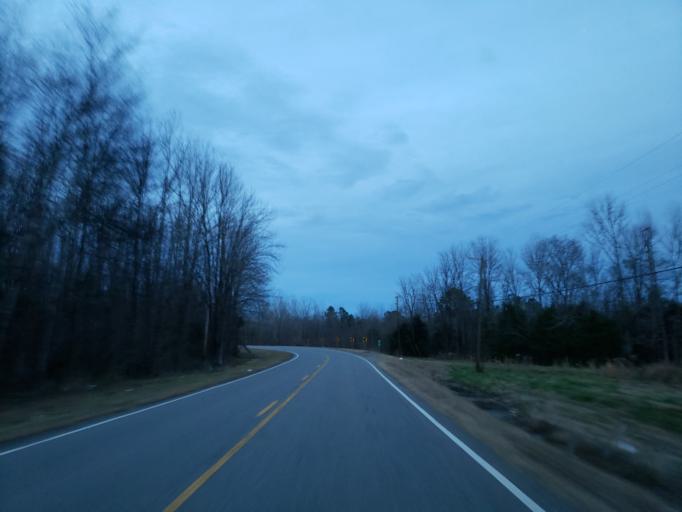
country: US
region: Alabama
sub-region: Greene County
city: Eutaw
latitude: 32.8544
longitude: -88.1037
